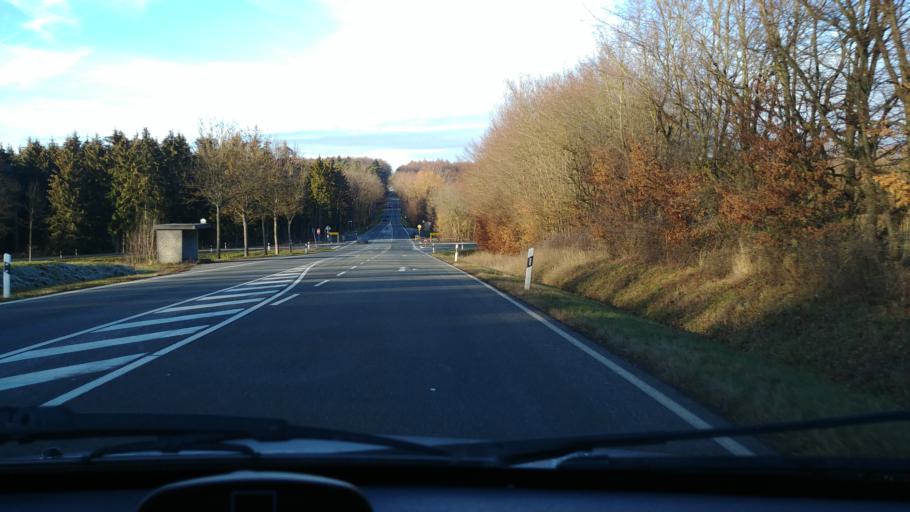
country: DE
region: Rheinland-Pfalz
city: Obertiefenbach
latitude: 50.2363
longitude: 7.8843
